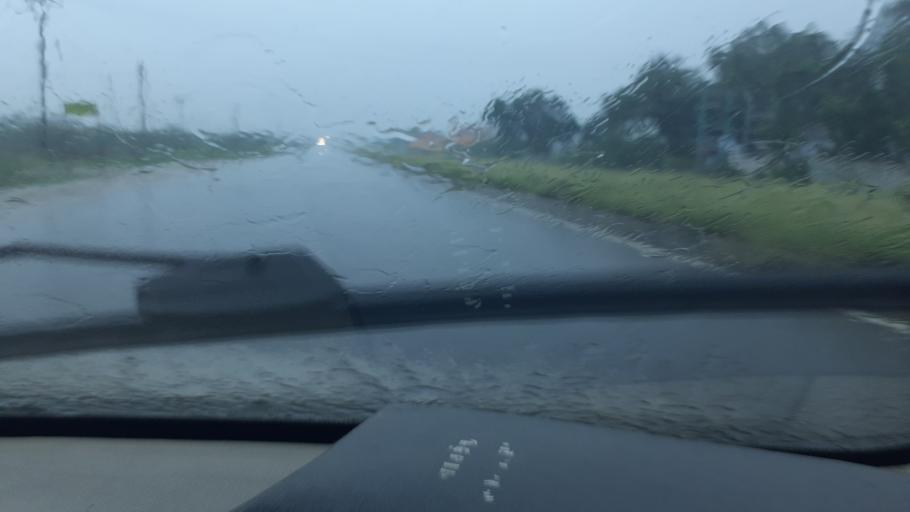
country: IN
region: Tamil Nadu
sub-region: Virudhunagar
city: Sattur
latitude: 9.4282
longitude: 77.9187
